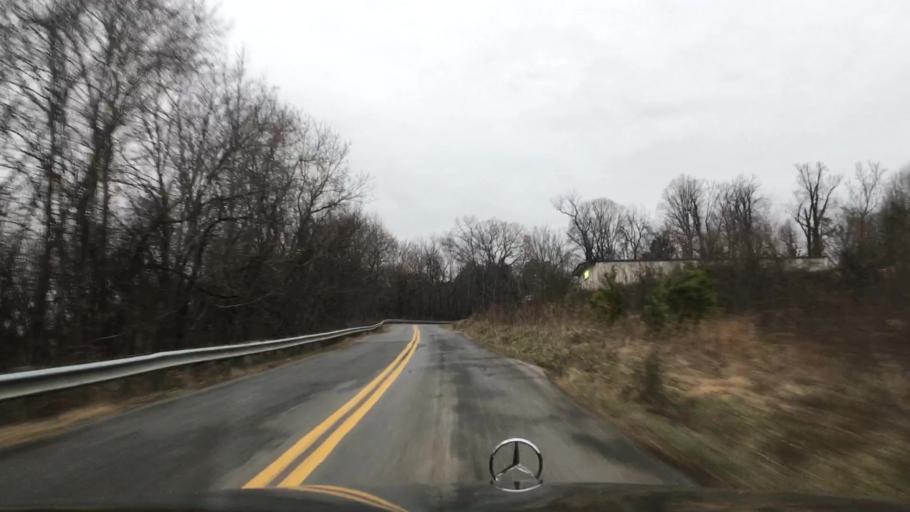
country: US
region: Virginia
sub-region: Pittsylvania County
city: Hurt
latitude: 37.1090
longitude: -79.3087
